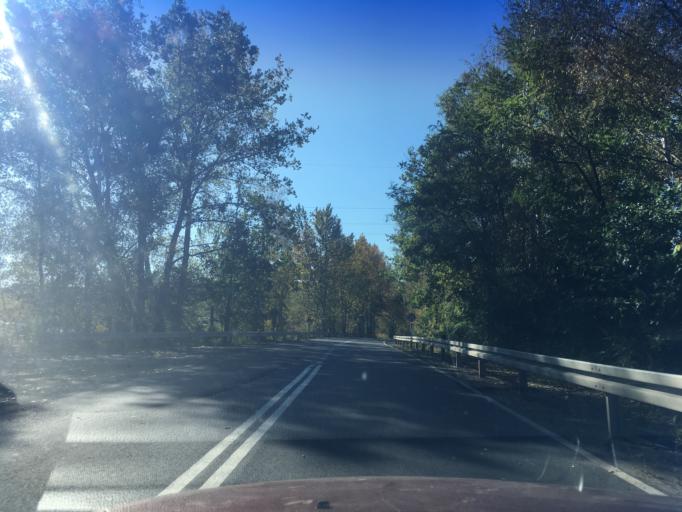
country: DE
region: Saxony
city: Hirschfelde
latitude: 50.9423
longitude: 14.8999
